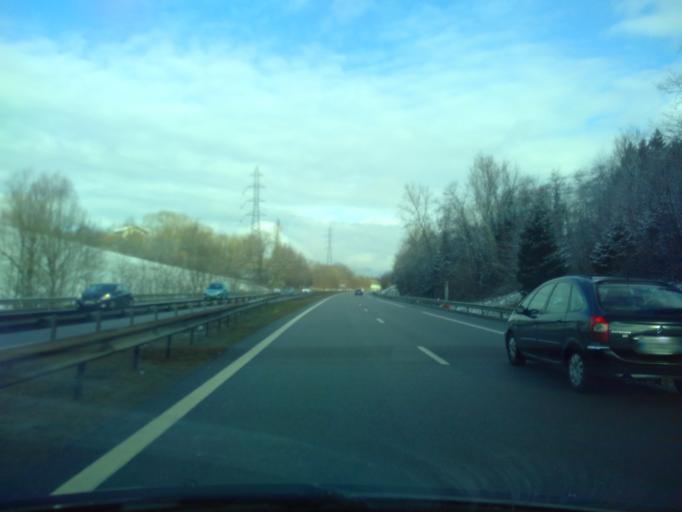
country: FR
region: Rhone-Alpes
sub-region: Departement de la Haute-Savoie
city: Chavanod
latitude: 45.8565
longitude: 6.0564
